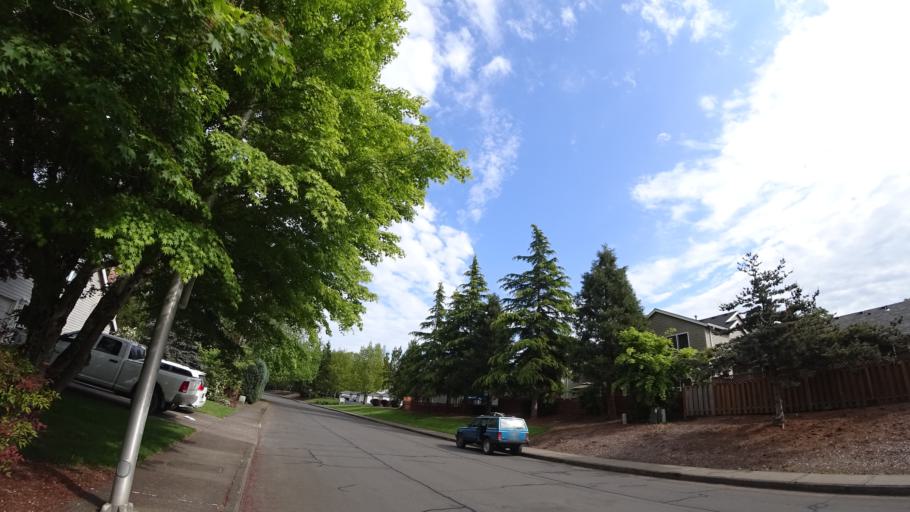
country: US
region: Oregon
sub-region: Washington County
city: Hillsboro
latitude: 45.4973
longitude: -122.9570
